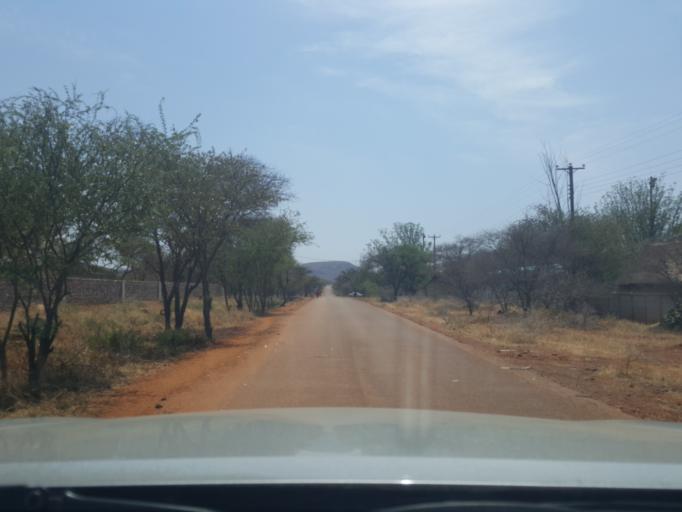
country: BW
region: South East
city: Ramotswa
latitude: -24.7731
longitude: 25.8452
